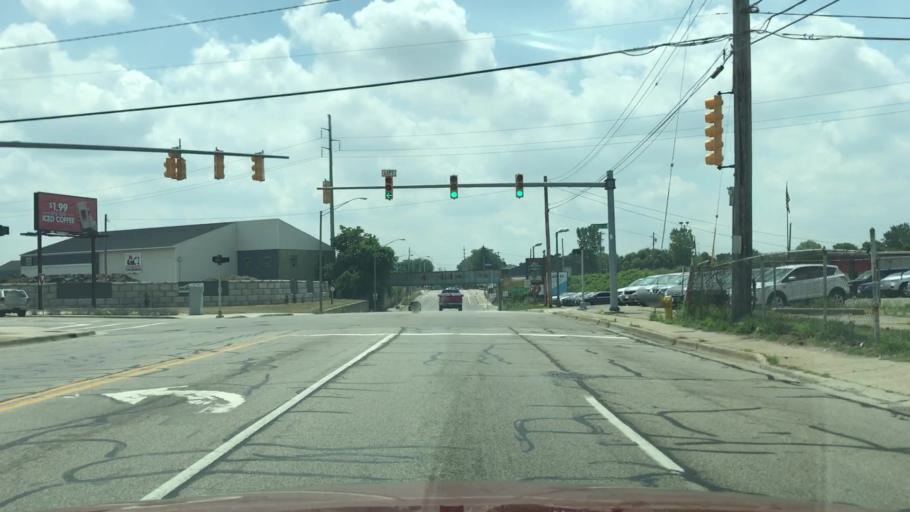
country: US
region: Michigan
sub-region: Kent County
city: Grand Rapids
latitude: 42.9999
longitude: -85.6885
